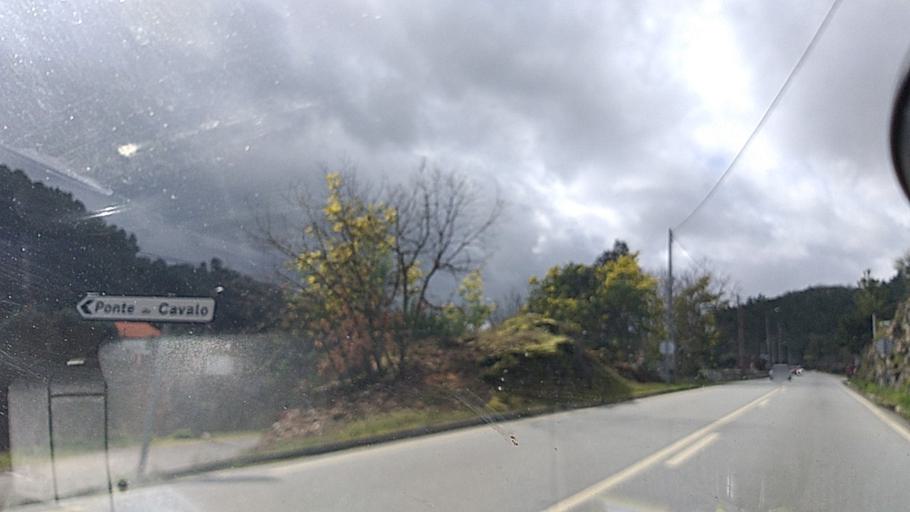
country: PT
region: Viseu
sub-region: Mangualde
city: Mangualde
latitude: 40.6429
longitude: -7.7376
